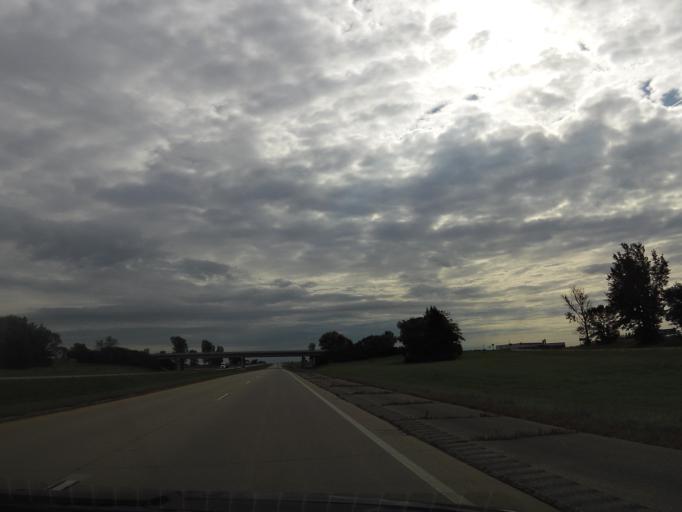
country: US
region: Minnesota
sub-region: Olmsted County
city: Eyota
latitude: 43.9550
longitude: -92.2418
